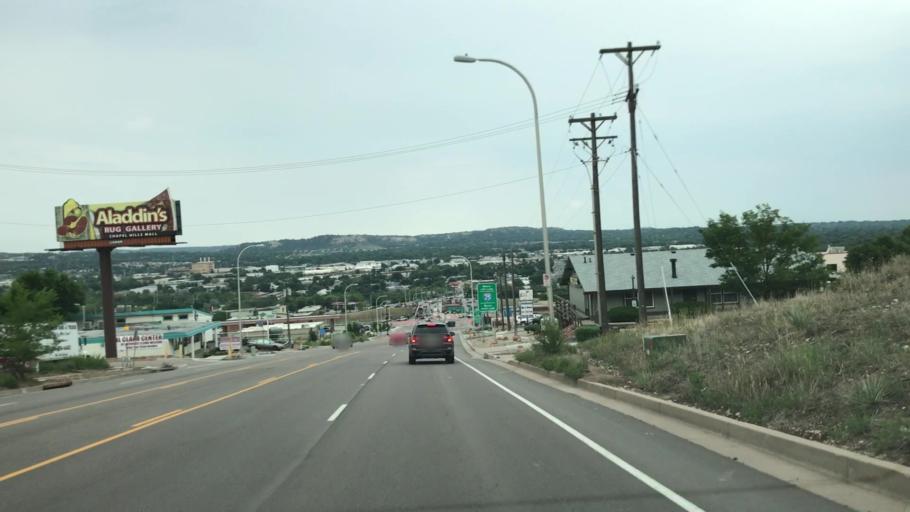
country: US
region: Colorado
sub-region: El Paso County
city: Colorado Springs
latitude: 38.8763
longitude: -104.8408
